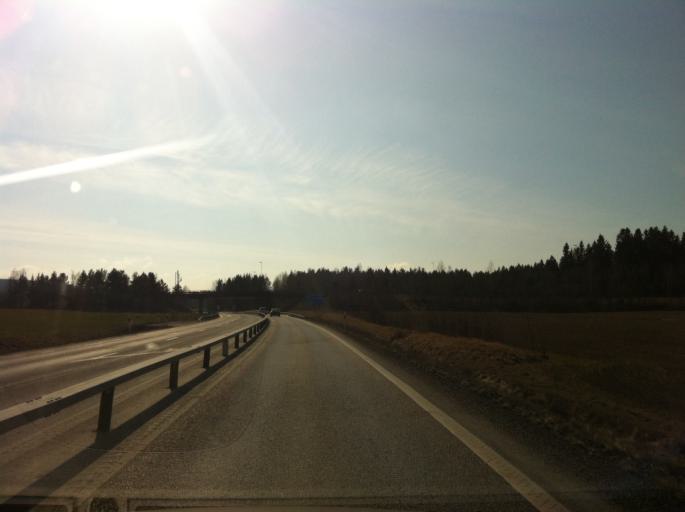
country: SE
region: Joenkoeping
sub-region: Jonkopings Kommun
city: Bankeryd
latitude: 57.8313
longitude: 14.1000
